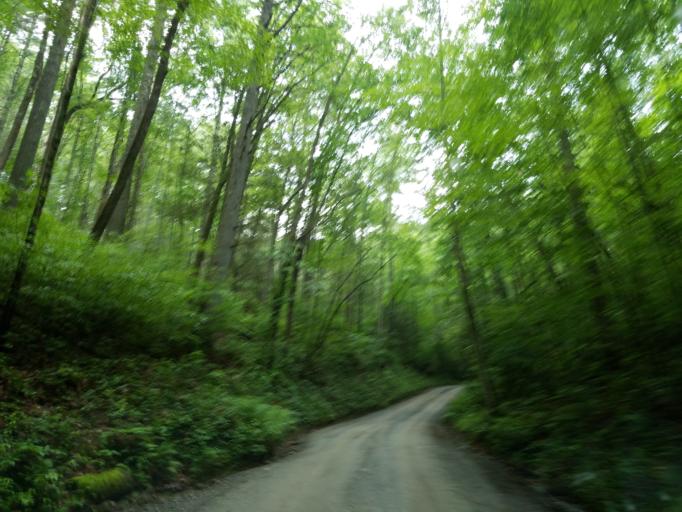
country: US
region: Georgia
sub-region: Fannin County
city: Blue Ridge
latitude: 34.7793
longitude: -84.3102
